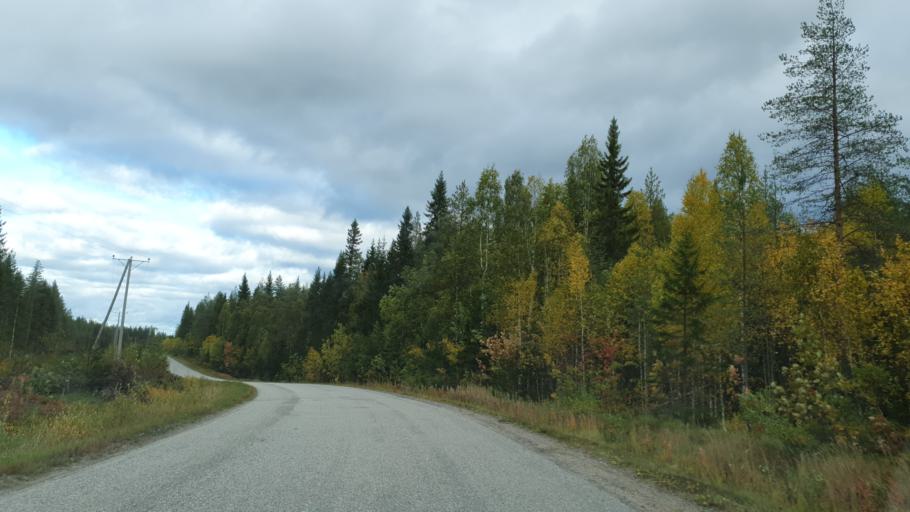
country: FI
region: Kainuu
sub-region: Kehys-Kainuu
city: Kuhmo
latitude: 63.9492
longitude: 29.8203
